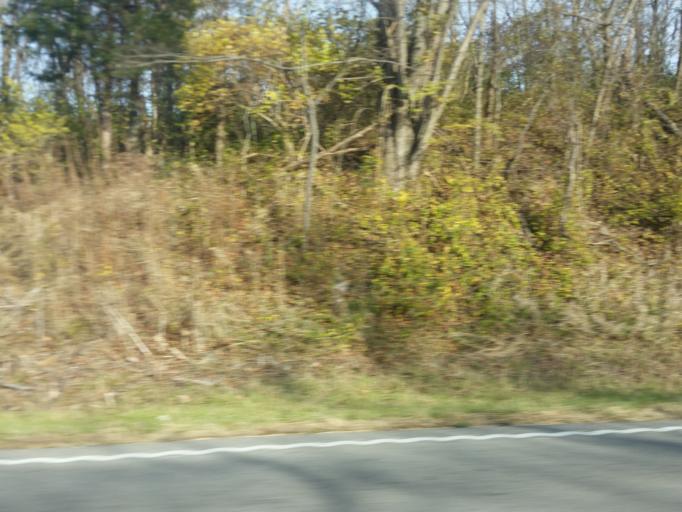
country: US
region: Kentucky
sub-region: Pendleton County
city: Falmouth
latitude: 38.7181
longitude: -84.3726
